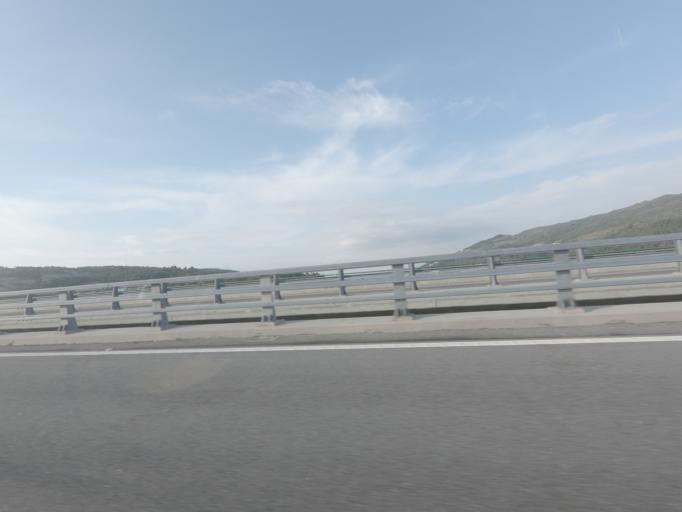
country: PT
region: Vila Real
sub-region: Vila Pouca de Aguiar
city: Vila Pouca de Aguiar
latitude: 41.4837
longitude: -7.6565
